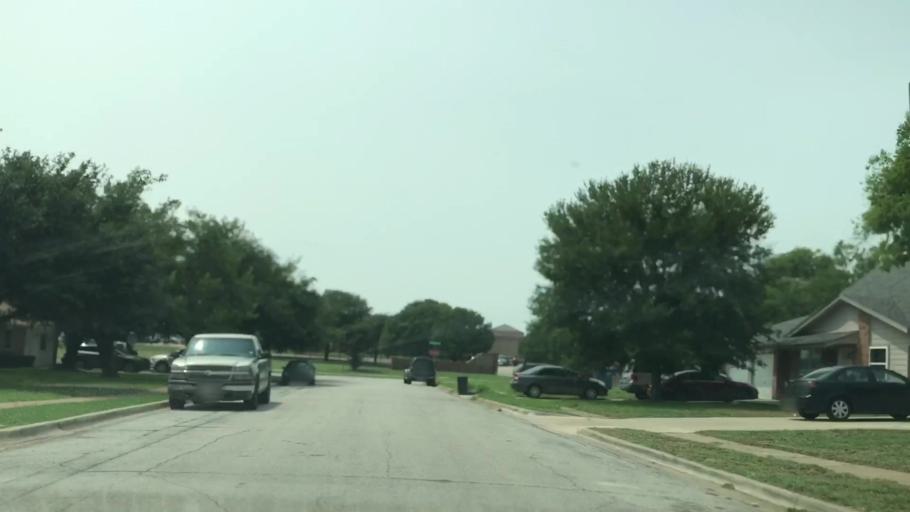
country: US
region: Texas
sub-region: Dallas County
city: Irving
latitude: 32.8394
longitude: -97.0057
